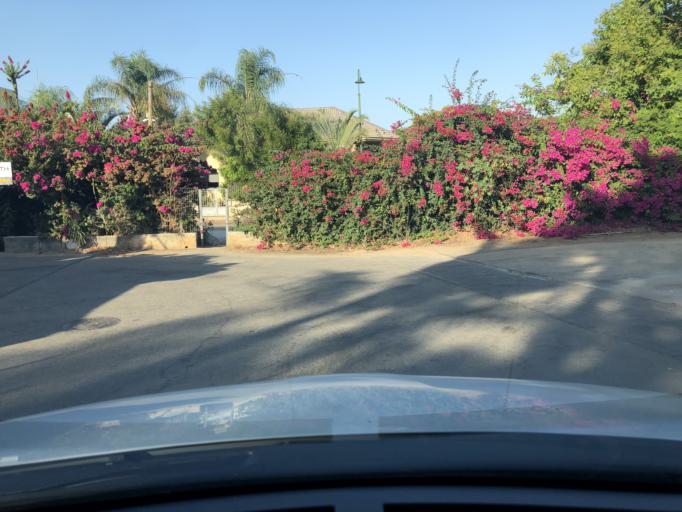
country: IL
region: Central District
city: Hod HaSharon
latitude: 32.1438
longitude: 34.9042
